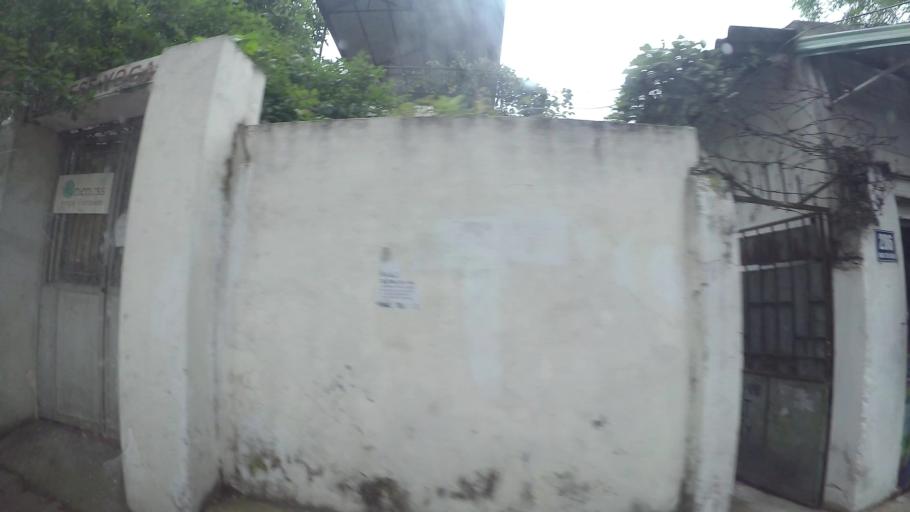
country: VN
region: Ha Noi
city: Dong Da
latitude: 21.0169
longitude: 105.8176
